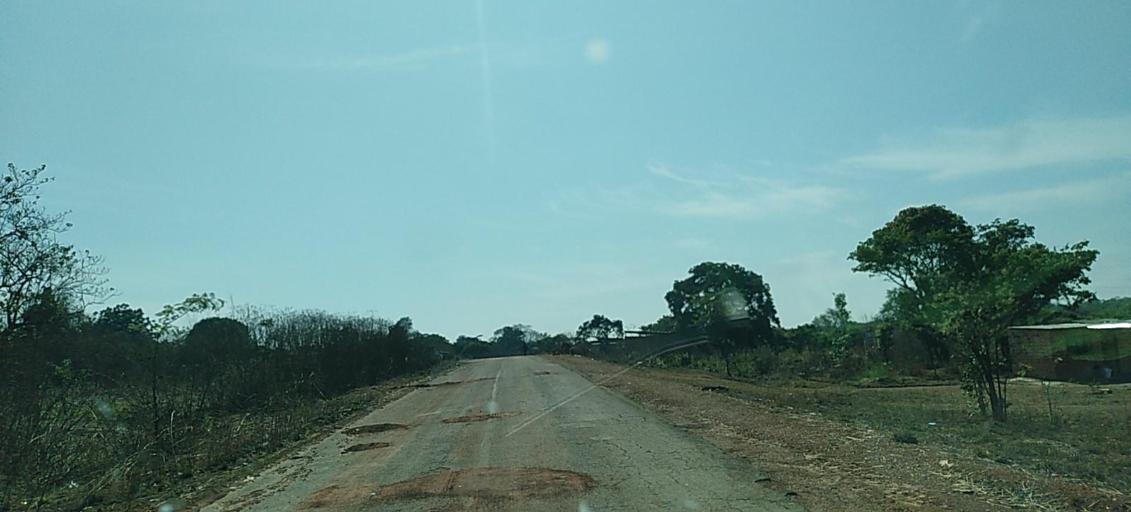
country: ZM
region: North-Western
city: Mwinilunga
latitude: -11.8254
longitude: 25.1352
